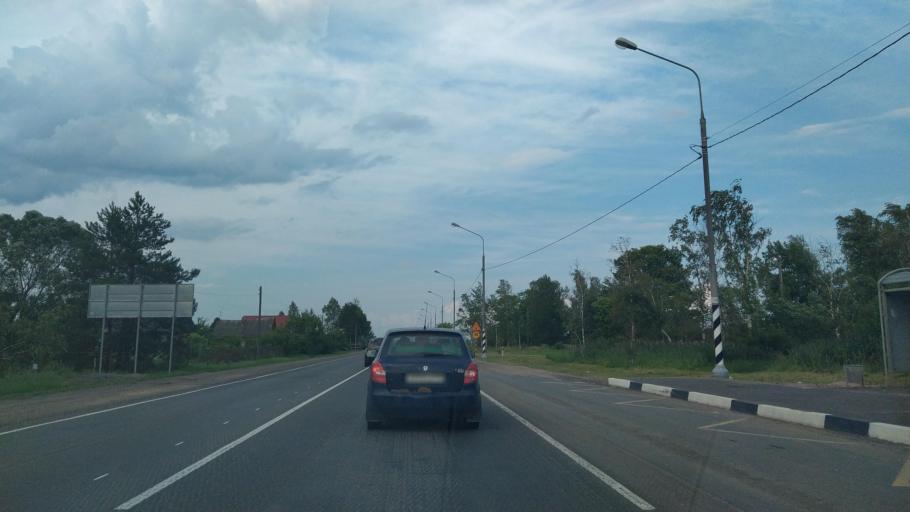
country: RU
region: Novgorod
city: Pankovka
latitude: 58.3864
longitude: 31.0231
